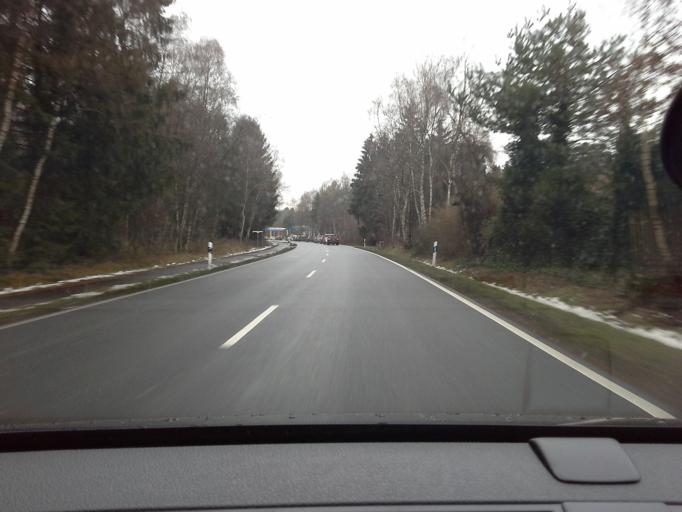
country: DE
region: Schleswig-Holstein
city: Henstedt-Ulzburg
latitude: 53.7474
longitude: 10.0025
